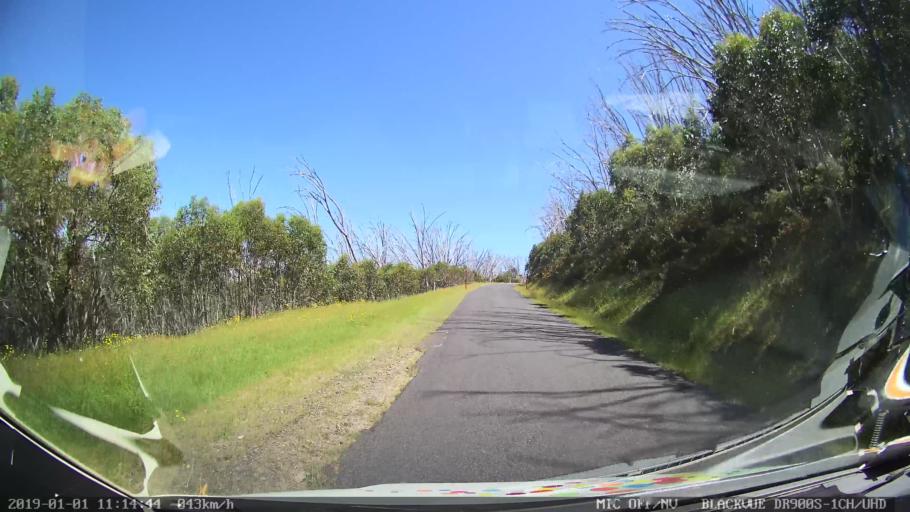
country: AU
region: New South Wales
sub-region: Snowy River
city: Jindabyne
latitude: -35.9495
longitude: 148.3875
